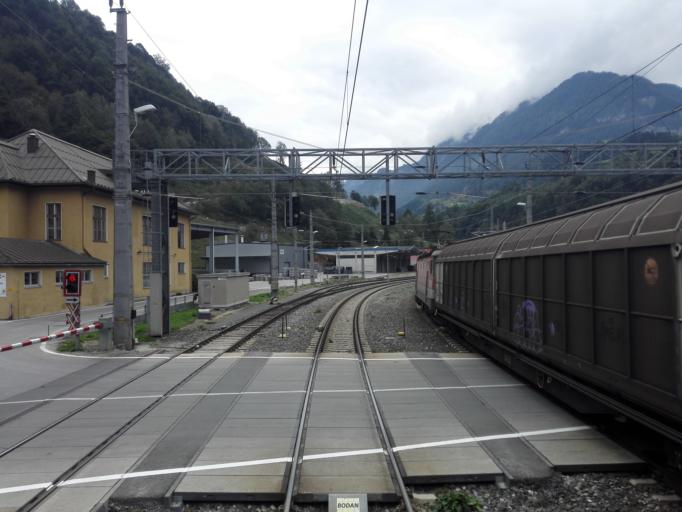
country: AT
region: Salzburg
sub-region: Politischer Bezirk Zell am See
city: Lend
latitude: 47.2982
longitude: 13.0521
